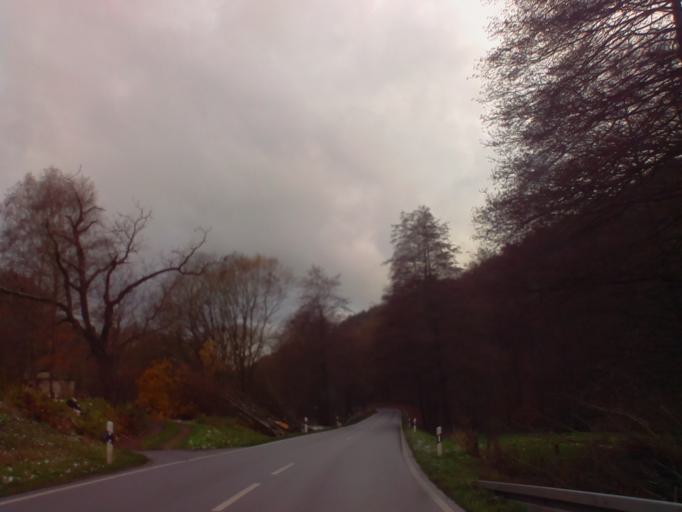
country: DE
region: Hesse
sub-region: Regierungsbezirk Darmstadt
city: Wald-Michelbach
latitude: 49.5710
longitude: 8.7943
